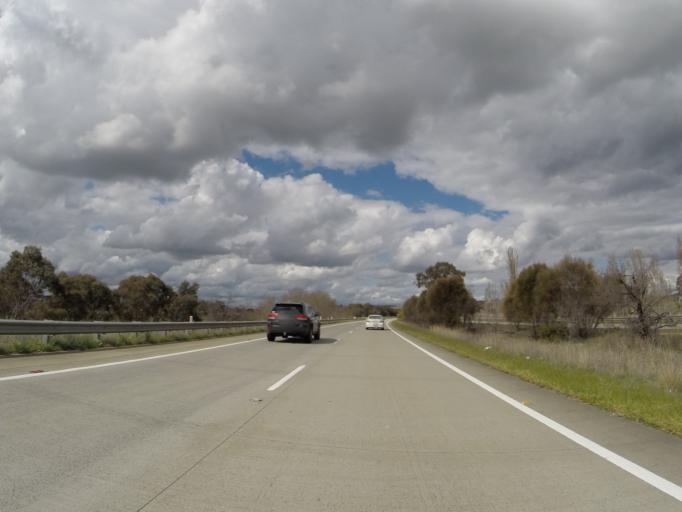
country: AU
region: New South Wales
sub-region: Yass Valley
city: Murrumbateman
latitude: -34.7864
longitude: 149.1840
